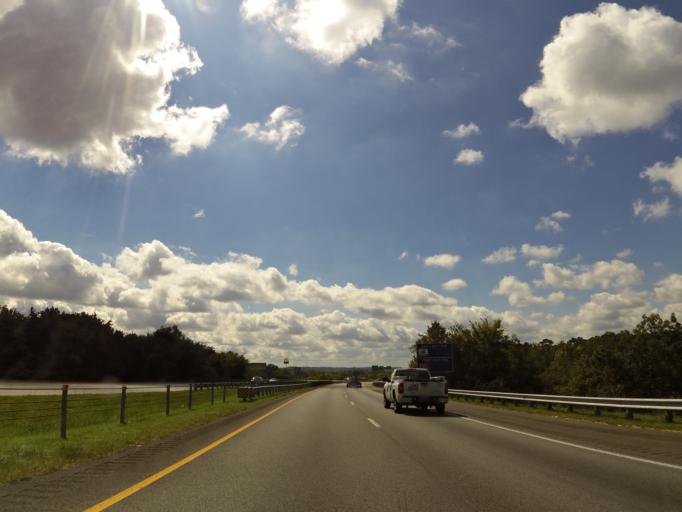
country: US
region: Alabama
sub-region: Jefferson County
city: Brighton
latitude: 33.4324
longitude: -86.9535
